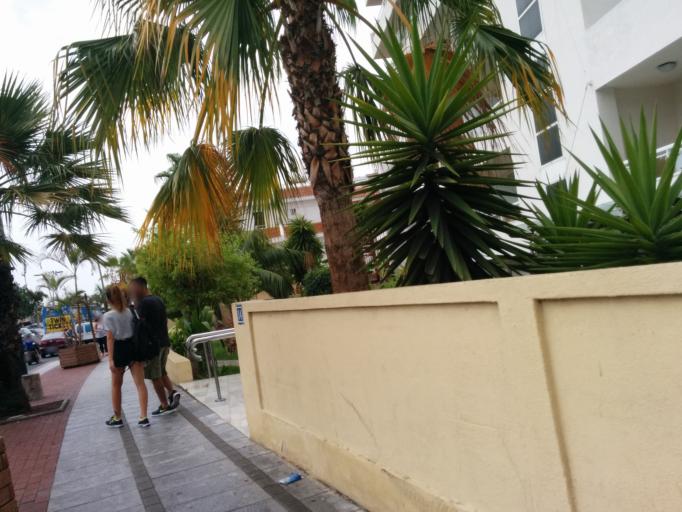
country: ES
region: Canary Islands
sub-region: Provincia de Santa Cruz de Tenerife
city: Playa de las Americas
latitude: 28.0633
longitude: -16.7268
